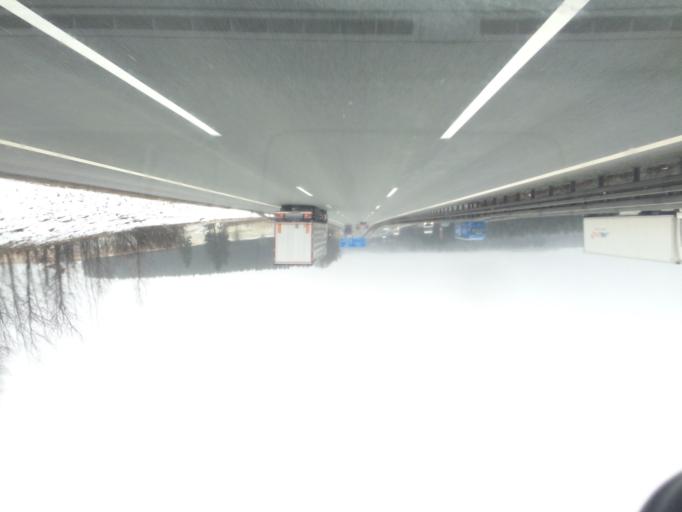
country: DE
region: Bavaria
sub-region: Upper Franconia
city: Leupoldsgrun
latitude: 50.2996
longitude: 11.8073
